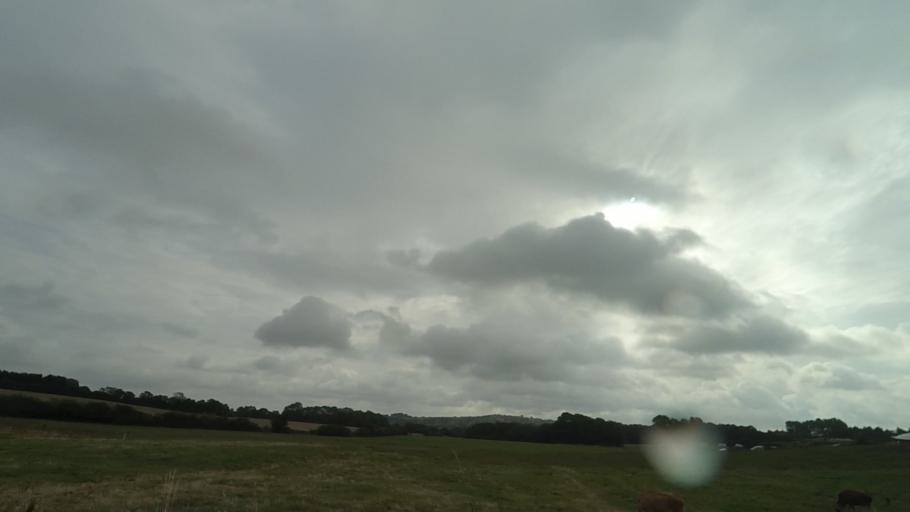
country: DK
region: Central Jutland
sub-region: Syddjurs Kommune
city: Ronde
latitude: 56.3010
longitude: 10.4450
